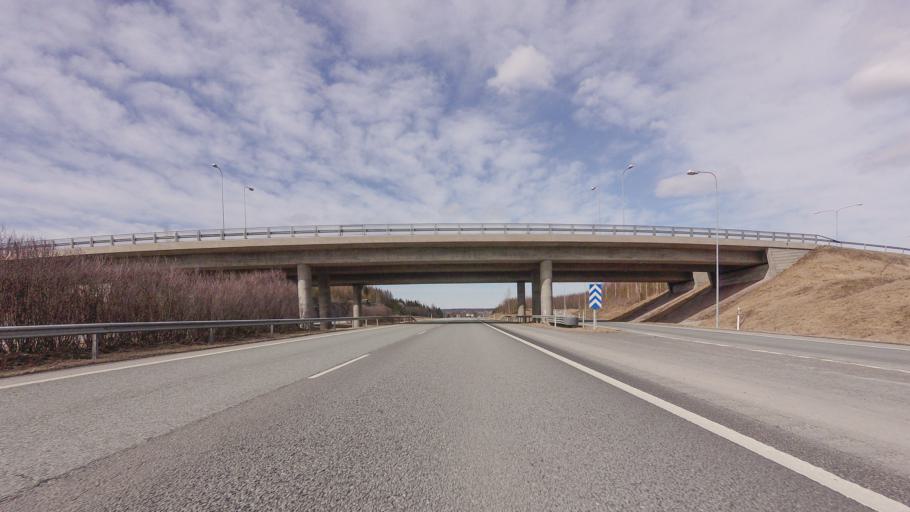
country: FI
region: Pirkanmaa
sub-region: Tampere
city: Lempaeaelae
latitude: 61.3316
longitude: 23.7990
